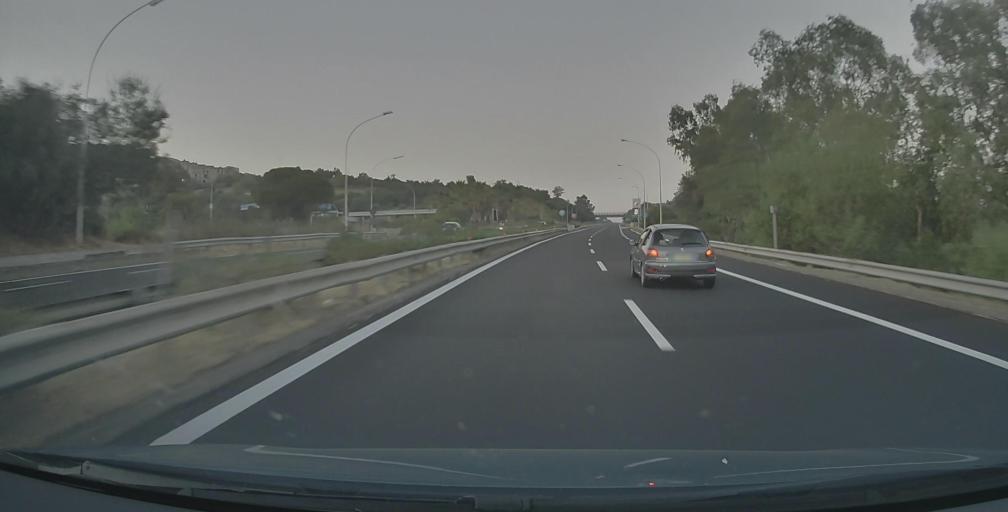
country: IT
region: Sicily
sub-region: Messina
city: Sant'Alessio Siculo
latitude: 37.9369
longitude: 15.3539
